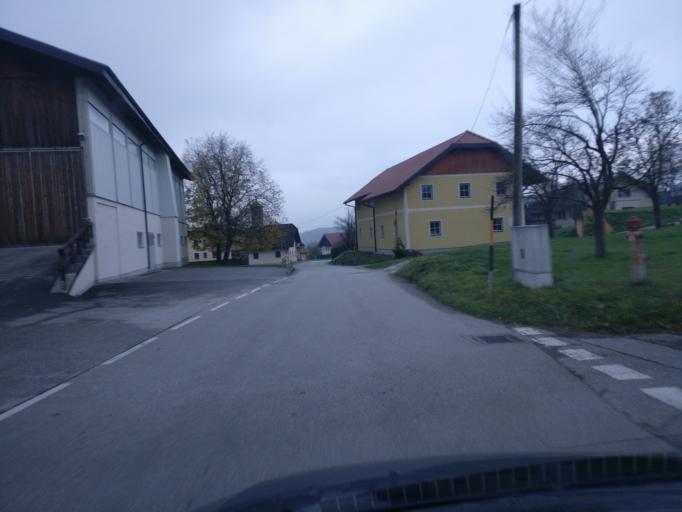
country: AT
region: Salzburg
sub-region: Politischer Bezirk Salzburg-Umgebung
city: Hallwang
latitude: 47.8491
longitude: 13.0996
